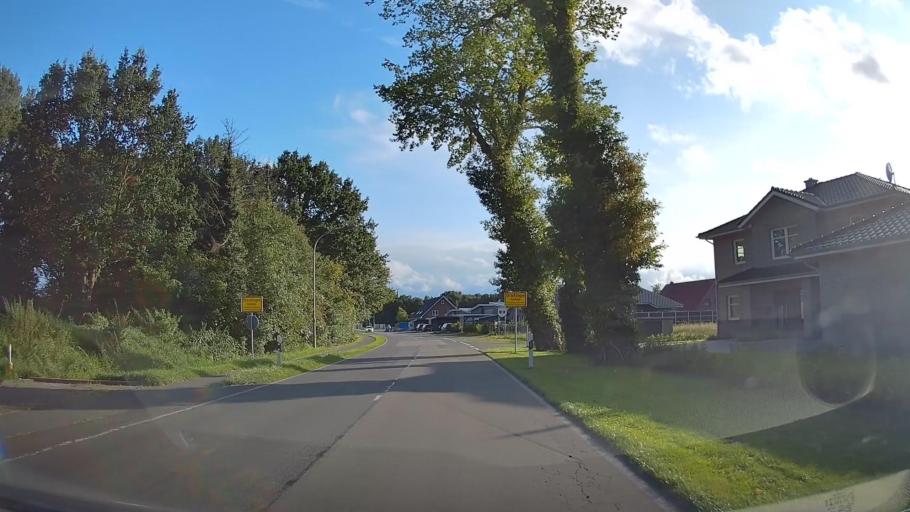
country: DE
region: Lower Saxony
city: Ostrhauderfehn
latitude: 53.1327
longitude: 7.6674
